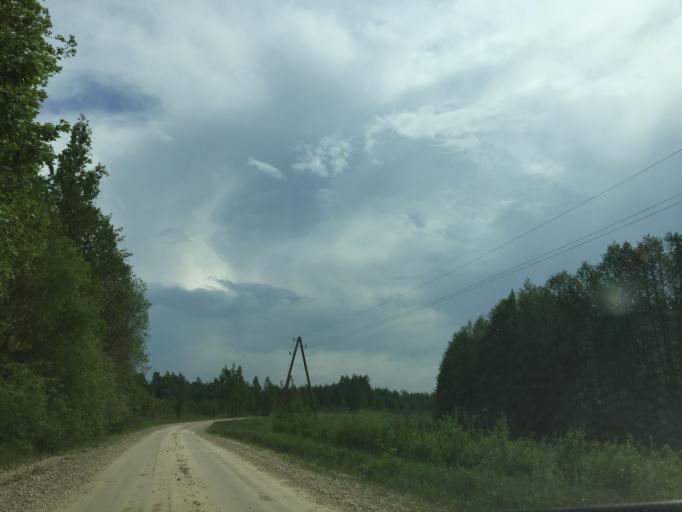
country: LV
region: Livani
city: Livani
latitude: 56.5774
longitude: 26.2174
